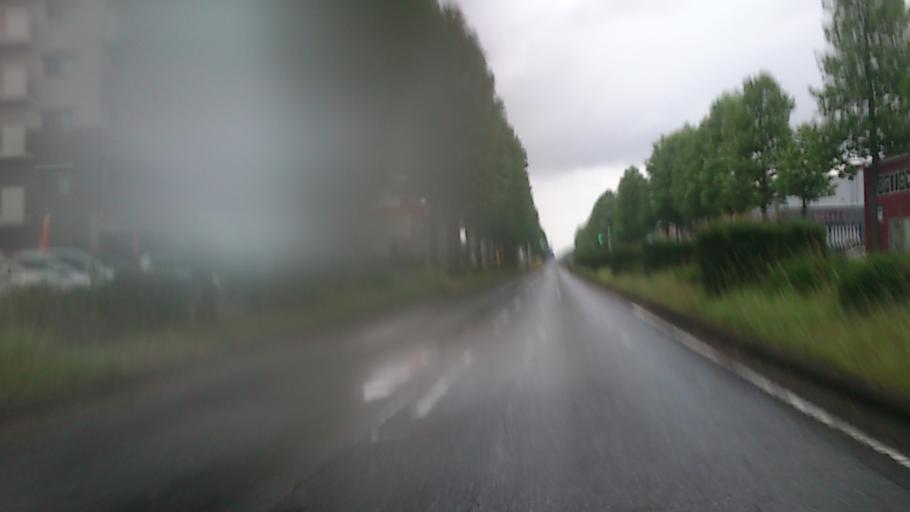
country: JP
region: Ibaraki
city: Naka
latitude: 36.0670
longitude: 140.1170
